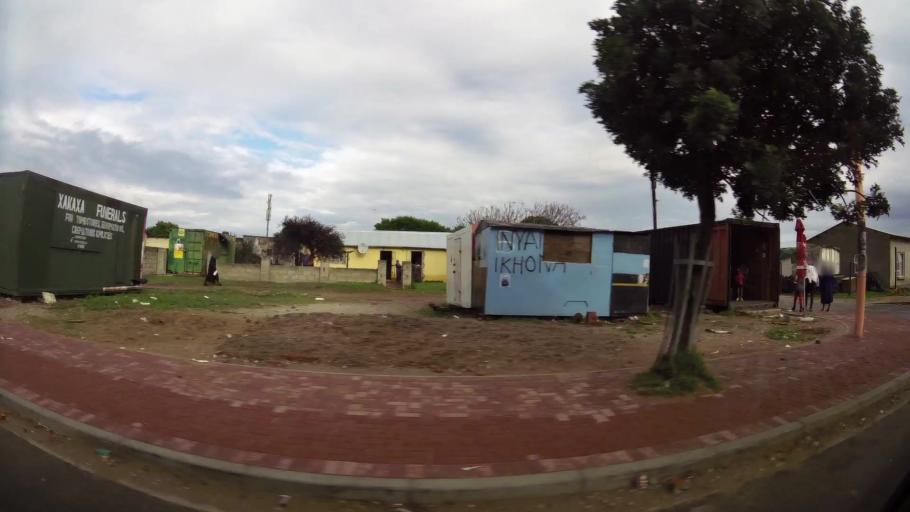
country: ZA
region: Eastern Cape
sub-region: Nelson Mandela Bay Metropolitan Municipality
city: Port Elizabeth
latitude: -33.9879
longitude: 25.5894
